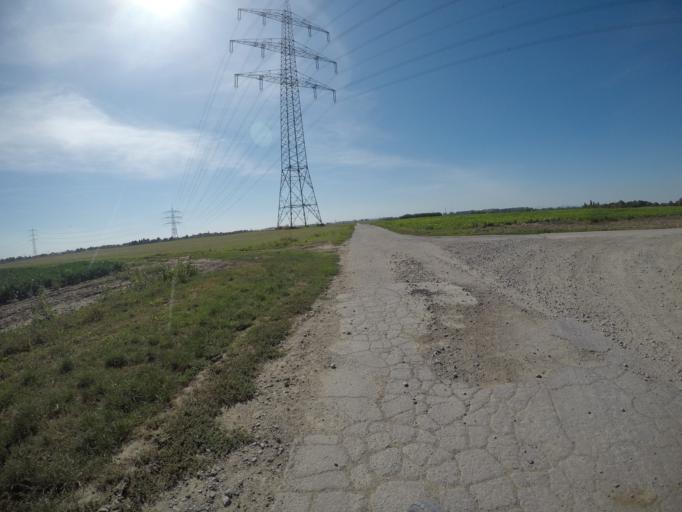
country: DE
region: Hesse
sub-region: Regierungsbezirk Darmstadt
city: Biblis
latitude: 49.6723
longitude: 8.4171
